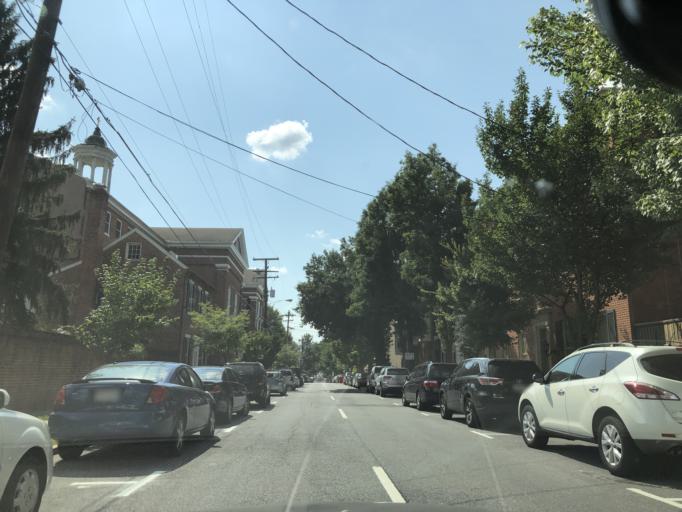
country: US
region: Maryland
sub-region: Frederick County
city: Frederick
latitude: 39.4163
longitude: -77.4062
